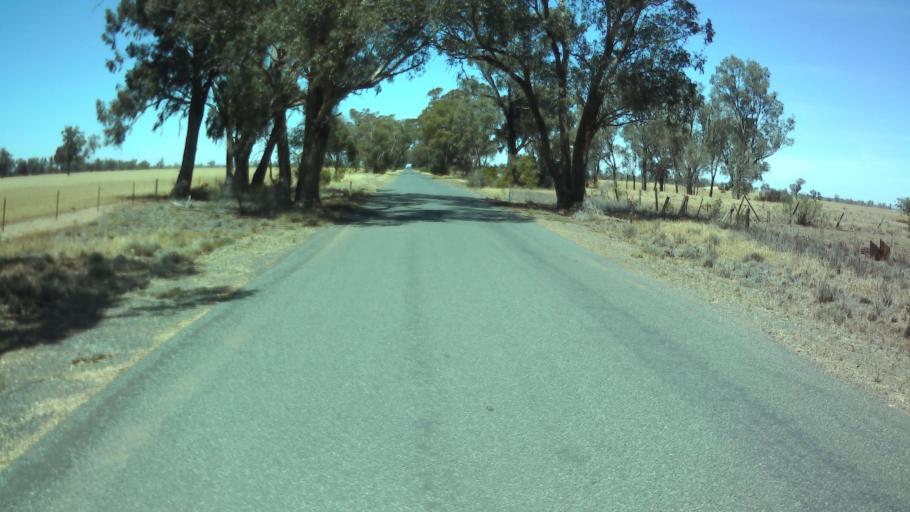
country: AU
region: New South Wales
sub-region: Weddin
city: Grenfell
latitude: -34.0166
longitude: 147.7935
